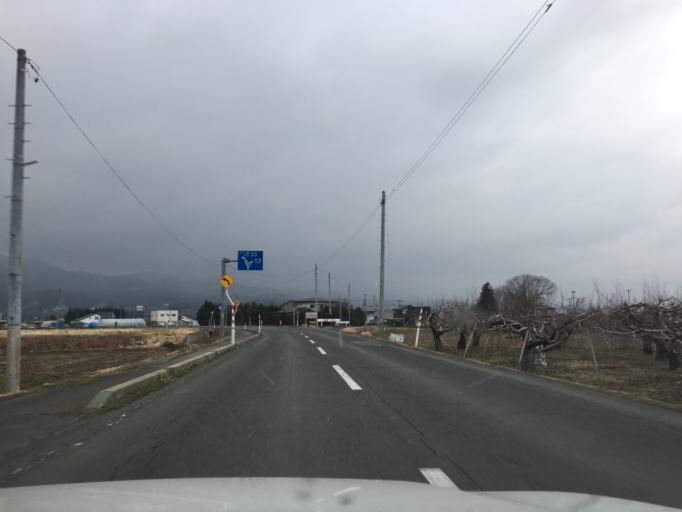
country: JP
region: Aomori
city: Hirosaki
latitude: 40.5602
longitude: 140.5483
